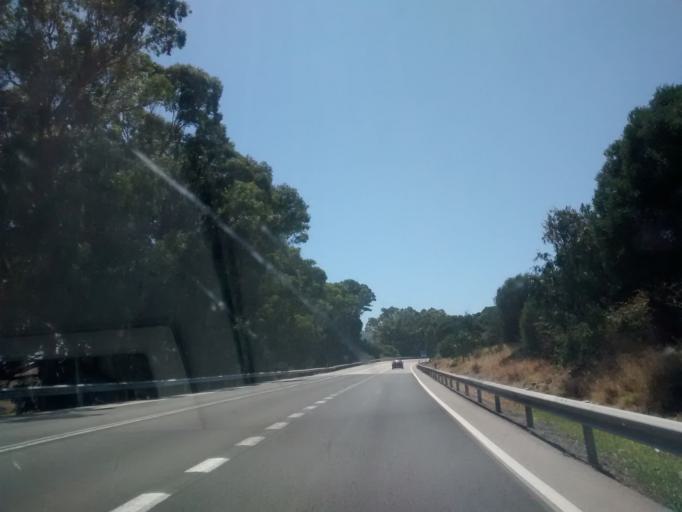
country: ES
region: Andalusia
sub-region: Provincia de Cadiz
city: Algeciras
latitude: 36.0906
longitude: -5.4809
